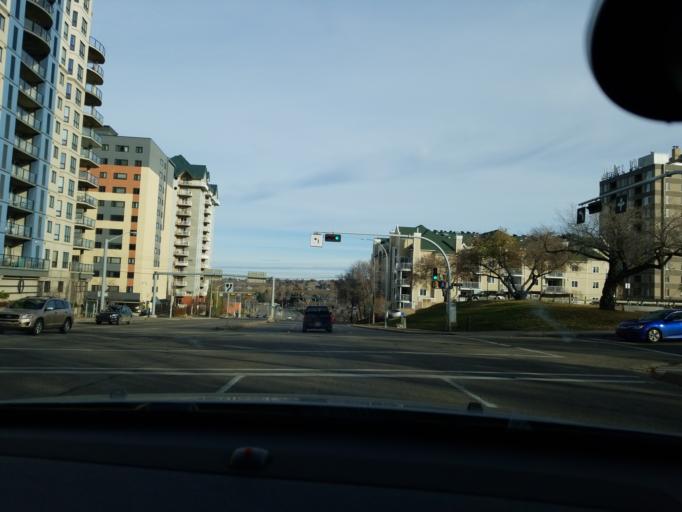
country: CA
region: Alberta
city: Edmonton
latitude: 53.5340
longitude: -113.5035
